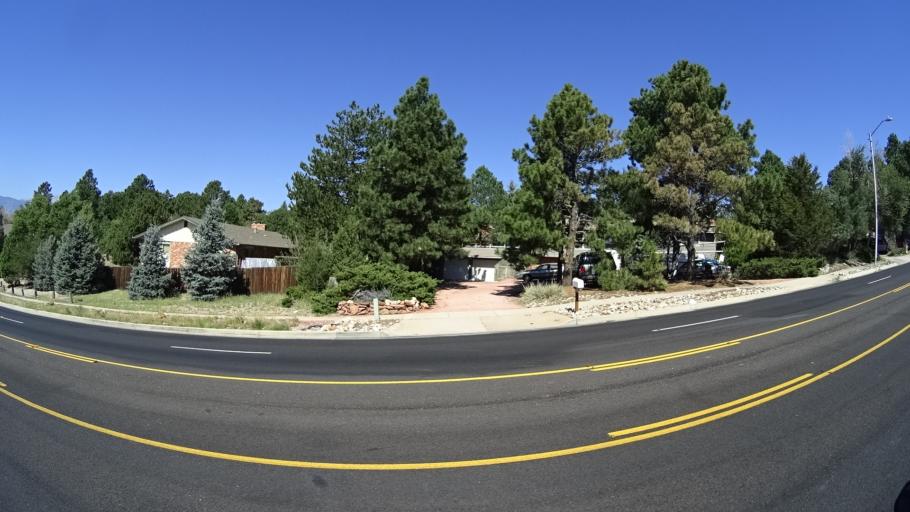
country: US
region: Colorado
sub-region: El Paso County
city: Cimarron Hills
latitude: 38.8650
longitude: -104.7417
